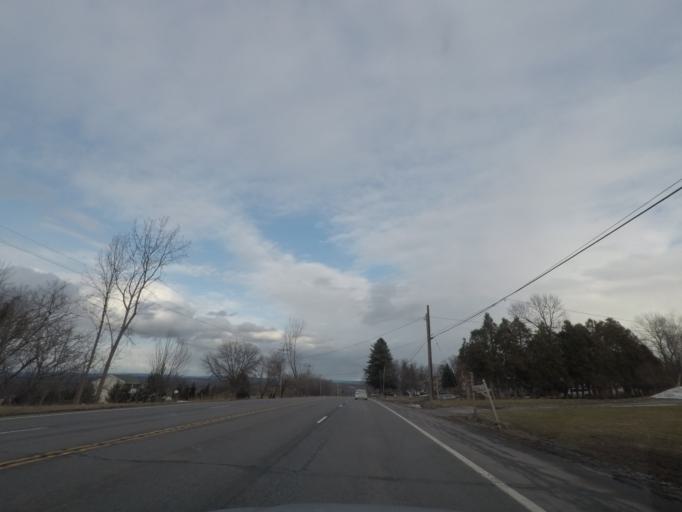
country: US
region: New York
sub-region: Oneida County
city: Clark Mills
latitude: 43.0804
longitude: -75.4068
